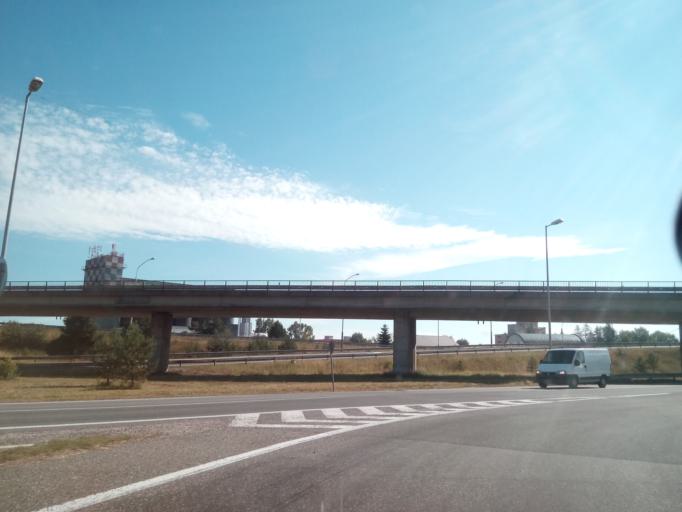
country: SK
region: Presovsky
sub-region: Okres Poprad
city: Poprad
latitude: 49.0597
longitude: 20.2692
